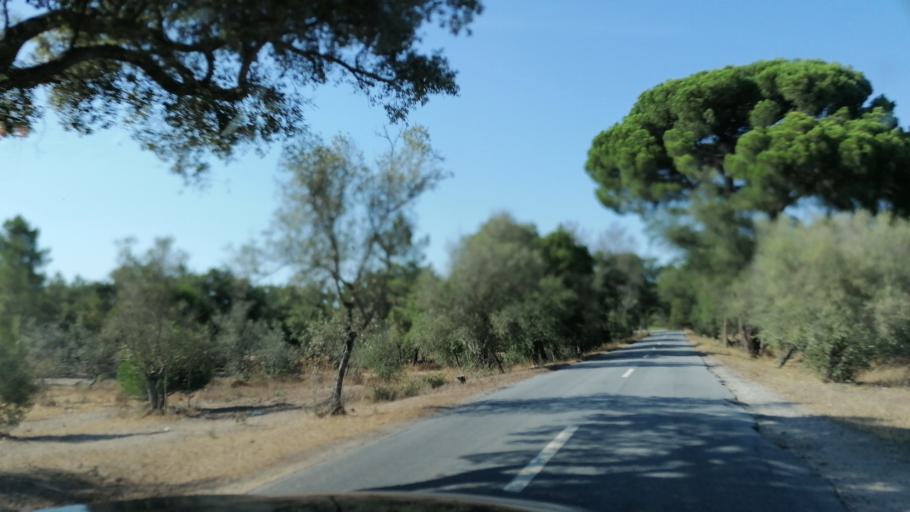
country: PT
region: Santarem
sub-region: Benavente
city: Poceirao
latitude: 38.7505
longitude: -8.6317
